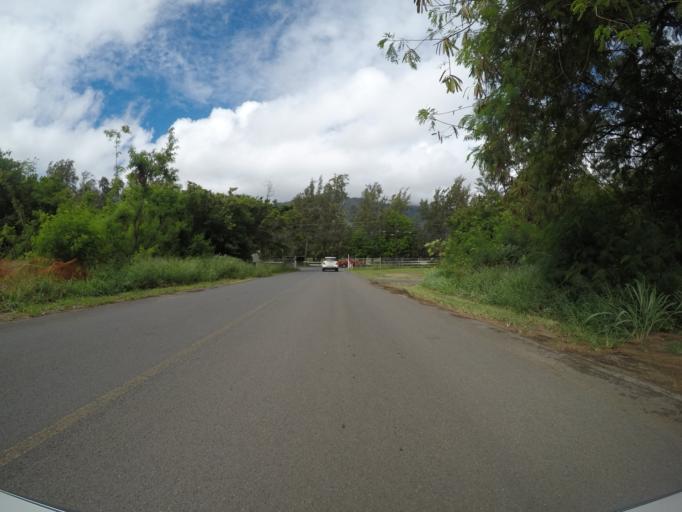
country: US
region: Hawaii
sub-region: Honolulu County
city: Waimanalo Beach
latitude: 21.3434
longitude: -157.7071
